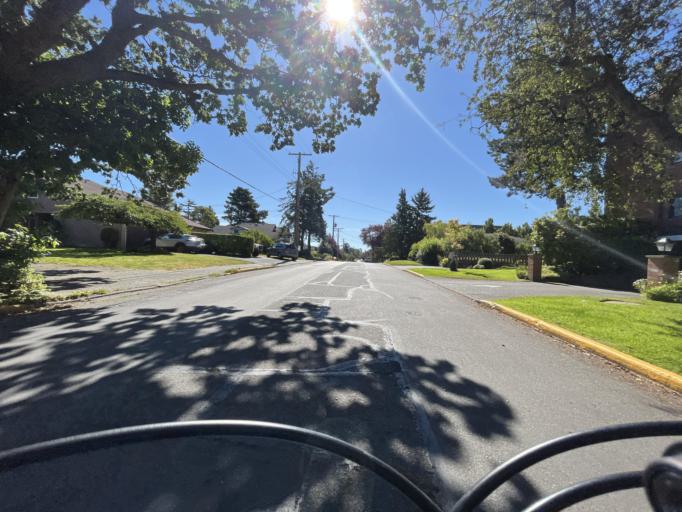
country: CA
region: British Columbia
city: Victoria
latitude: 48.4420
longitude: -123.3963
